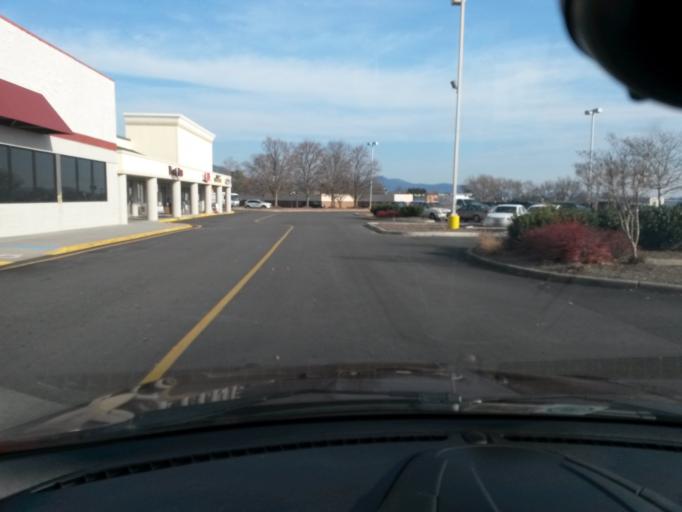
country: US
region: Virginia
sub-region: Roanoke County
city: Hollins
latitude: 37.3198
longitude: -79.9617
